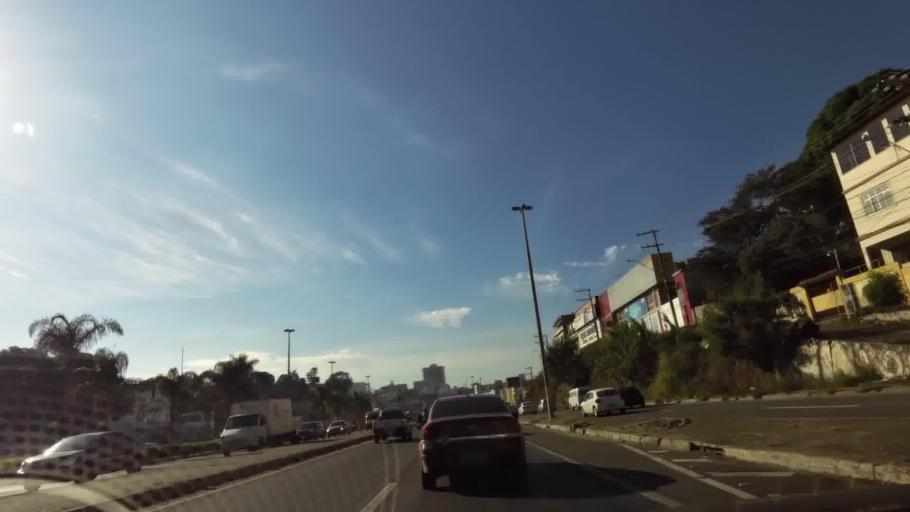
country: BR
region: Espirito Santo
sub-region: Vitoria
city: Vitoria
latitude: -20.3372
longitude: -40.3865
